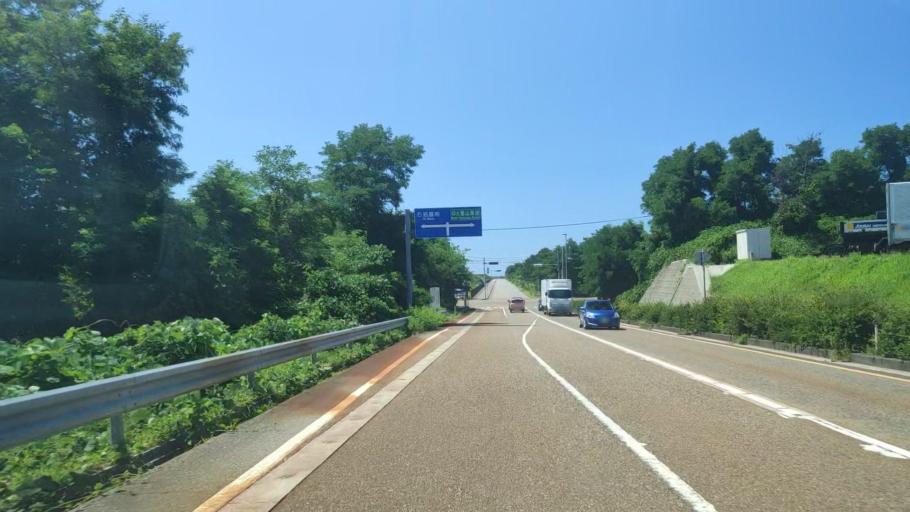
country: JP
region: Ishikawa
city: Kanazawa-shi
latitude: 36.6264
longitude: 136.6125
